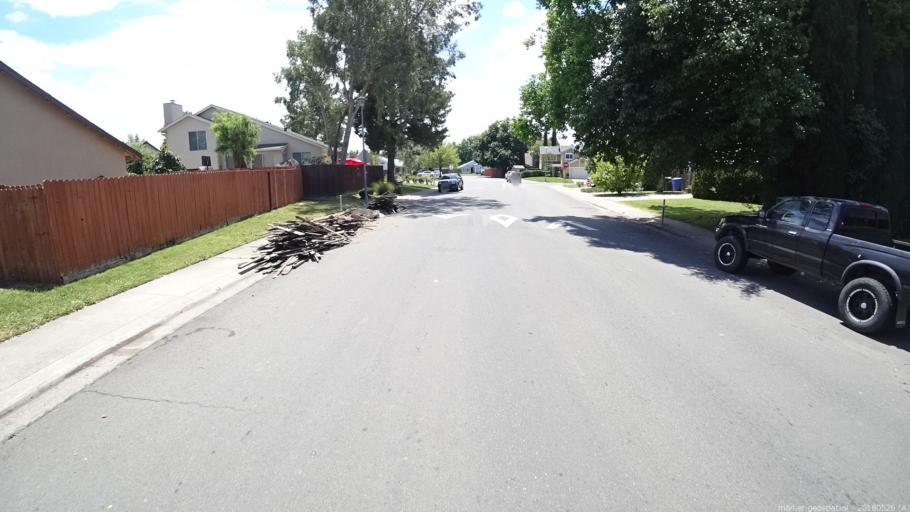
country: US
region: California
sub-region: Sacramento County
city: Sacramento
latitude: 38.6202
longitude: -121.4881
